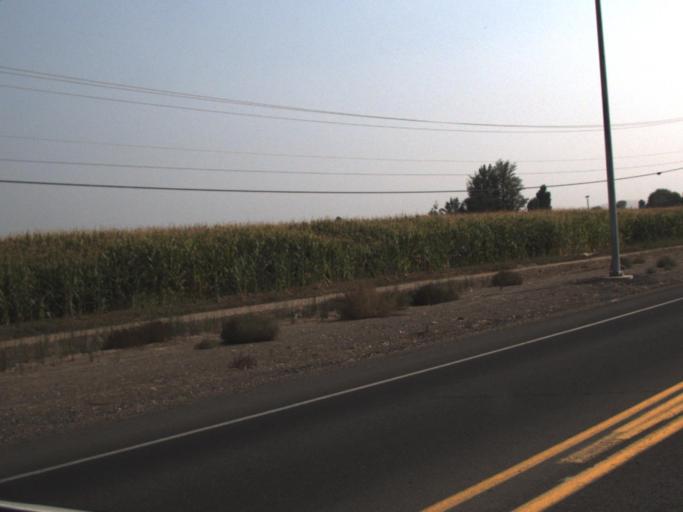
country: US
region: Washington
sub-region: Yakima County
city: Toppenish
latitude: 46.3910
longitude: -120.3146
